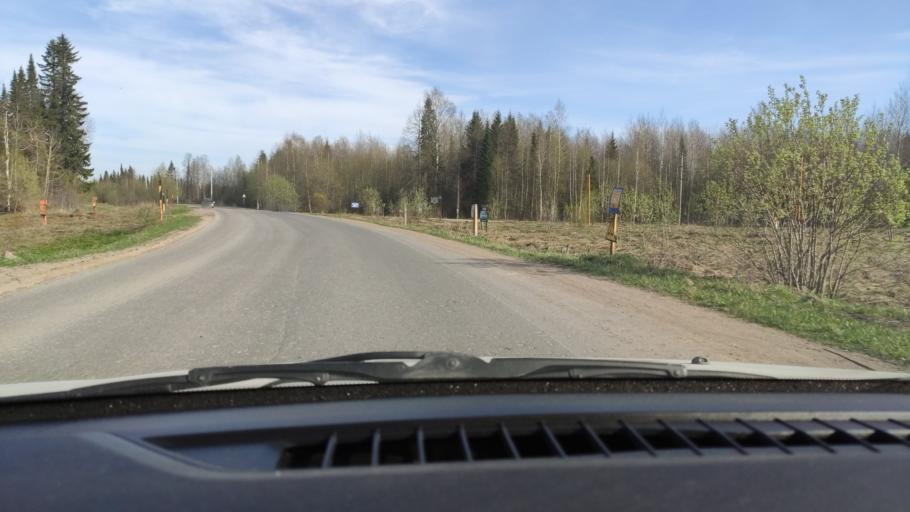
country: RU
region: Perm
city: Novyye Lyady
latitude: 57.9427
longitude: 56.5697
